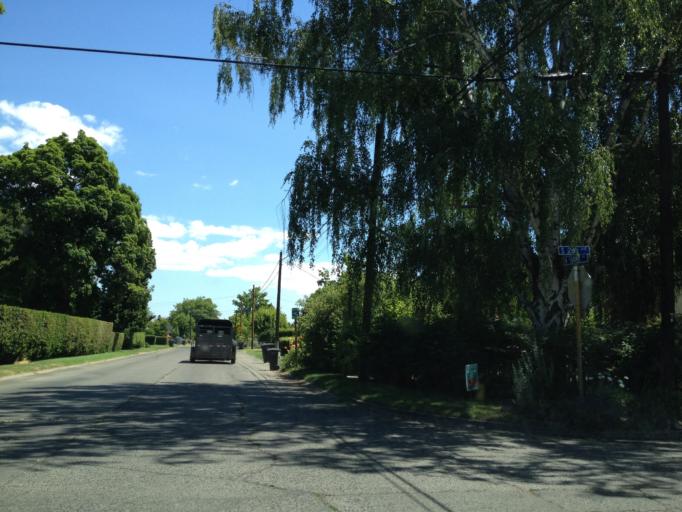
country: US
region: Washington
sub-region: Yakima County
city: Yakima
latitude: 46.5972
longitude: -120.5464
